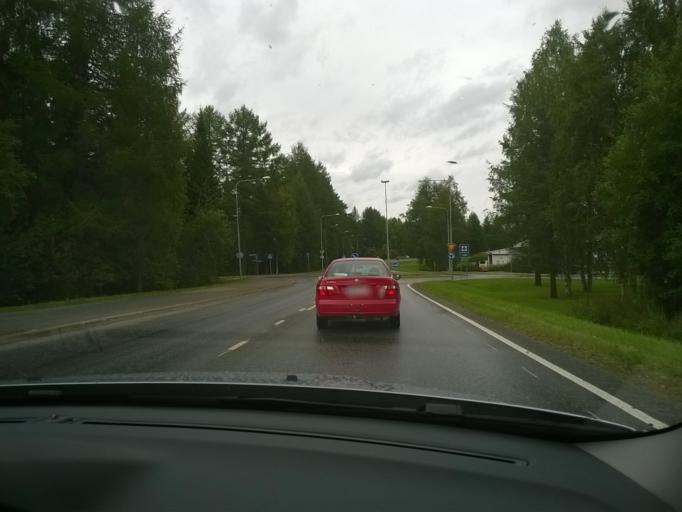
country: FI
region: Kainuu
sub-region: Kehys-Kainuu
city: Kuhmo
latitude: 64.1253
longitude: 29.5057
